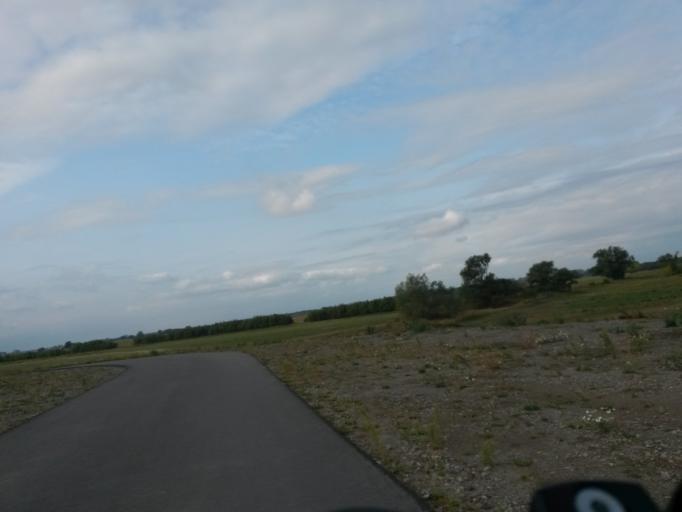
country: DE
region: Saxony-Anhalt
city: Tangermunde
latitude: 52.5378
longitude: 12.0031
